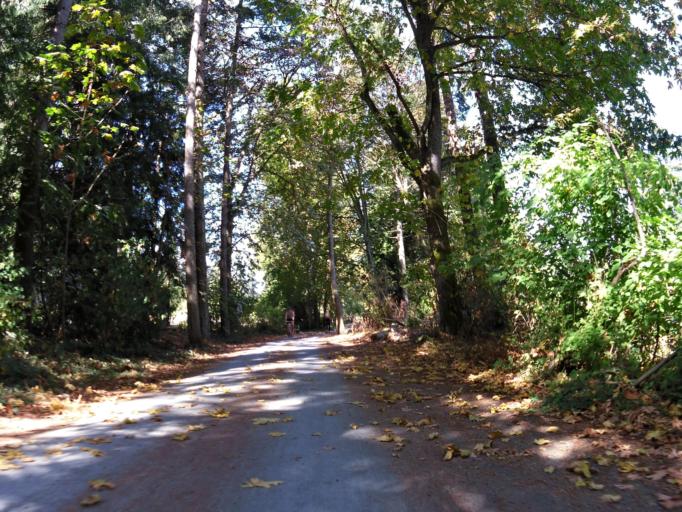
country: CA
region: British Columbia
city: Victoria
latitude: 48.5363
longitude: -123.3785
